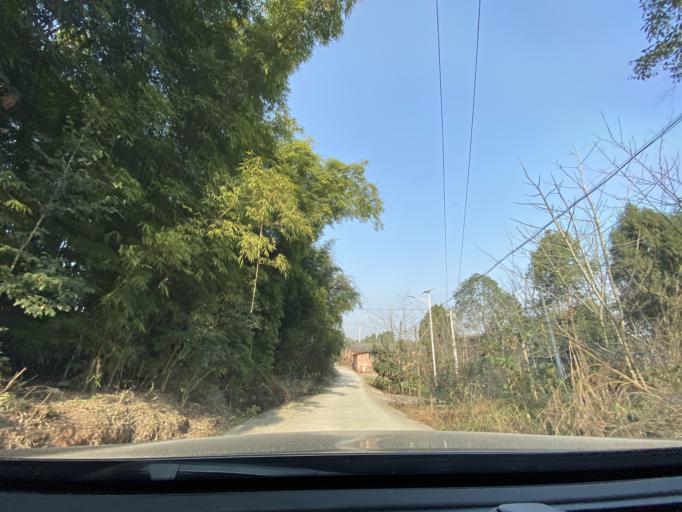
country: CN
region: Sichuan
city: Wenlin
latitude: 30.2487
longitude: 104.2490
